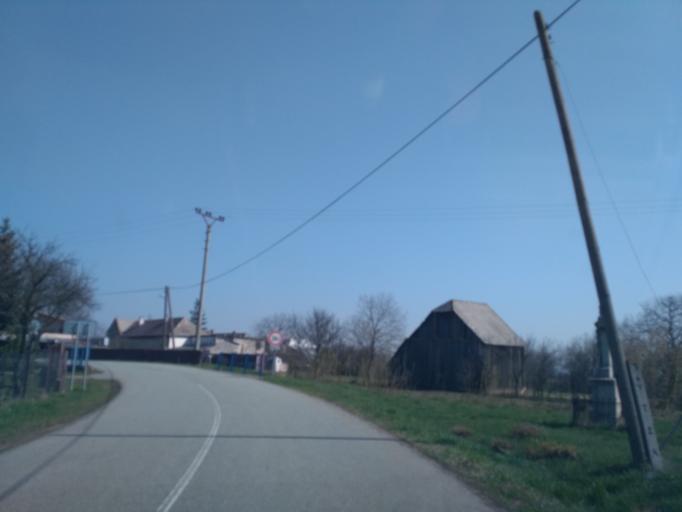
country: SK
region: Kosicky
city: Secovce
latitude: 48.7612
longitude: 21.6605
